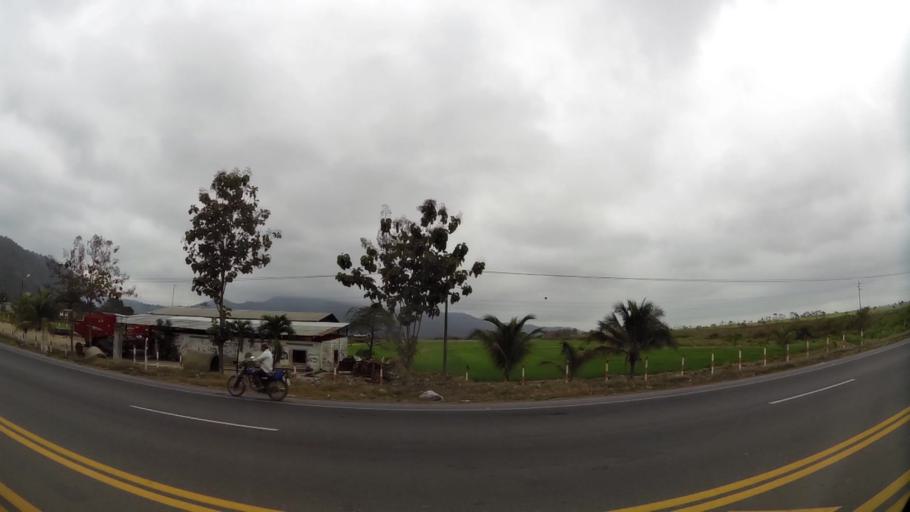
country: EC
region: Guayas
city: Naranjal
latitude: -2.4739
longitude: -79.6204
